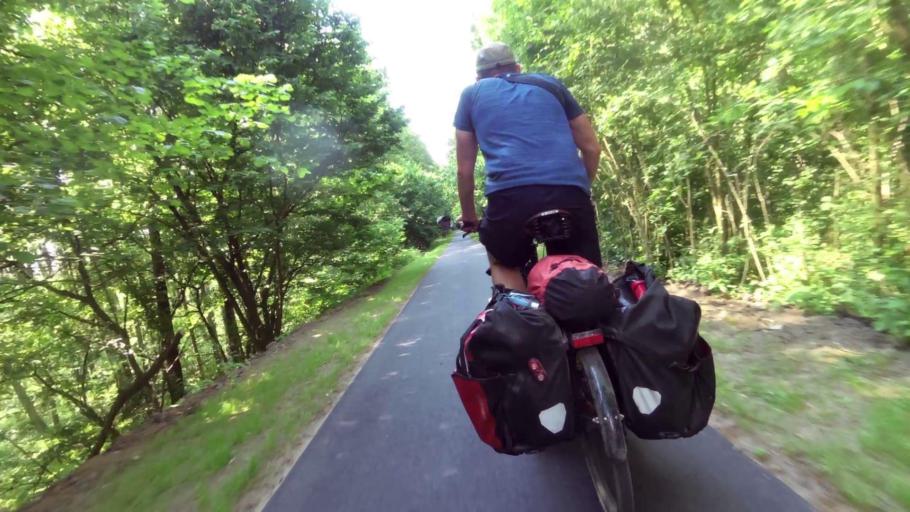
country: PL
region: West Pomeranian Voivodeship
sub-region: Powiat gryfinski
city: Gryfino
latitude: 53.2253
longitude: 14.5334
